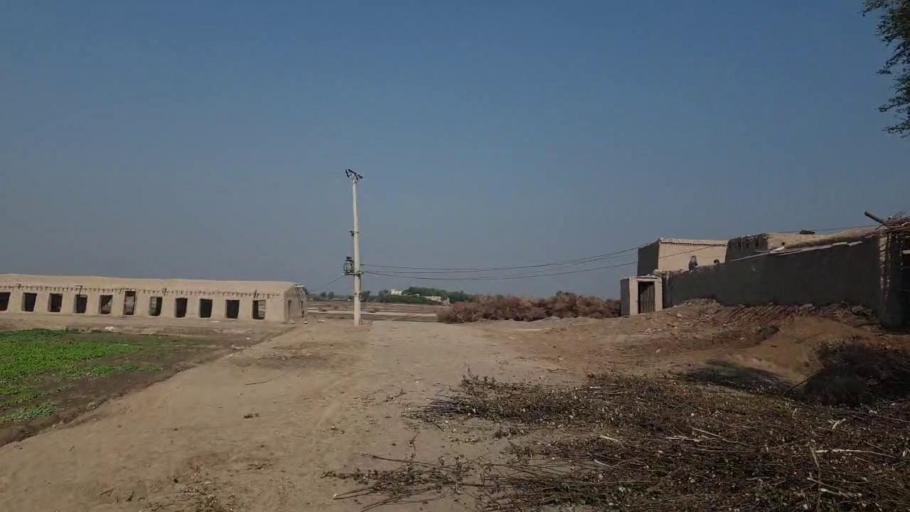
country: PK
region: Sindh
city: Sehwan
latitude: 26.4329
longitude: 67.7730
